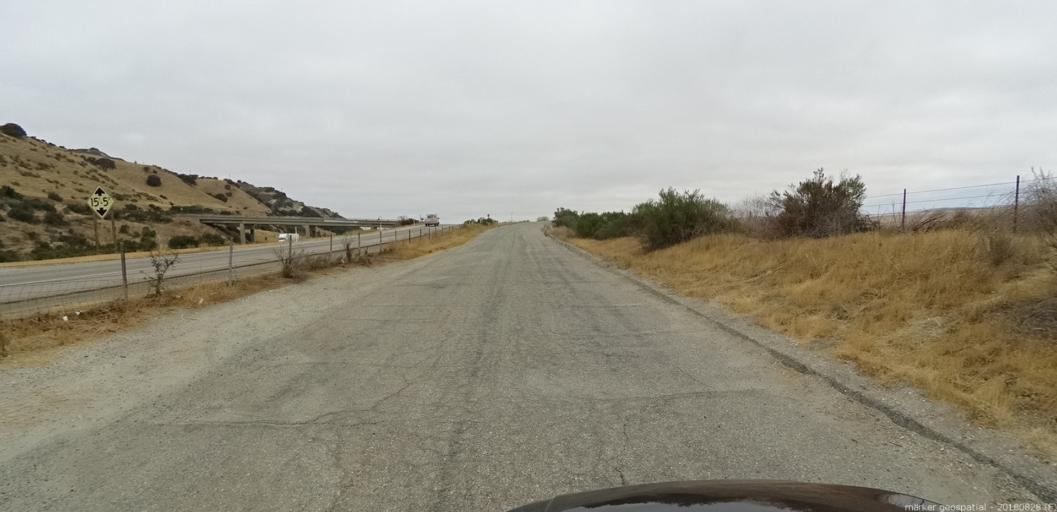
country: US
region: California
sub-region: San Luis Obispo County
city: Lake Nacimiento
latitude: 35.9453
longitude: -120.8743
